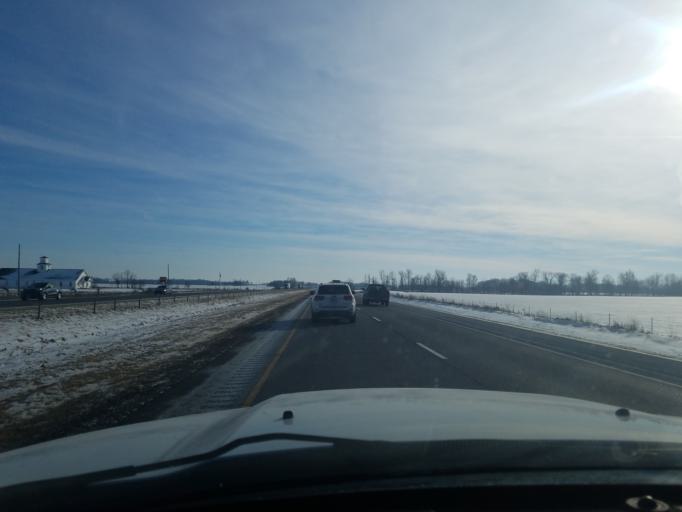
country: US
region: Indiana
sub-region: Madison County
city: Alexandria
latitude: 40.3207
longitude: -85.5589
